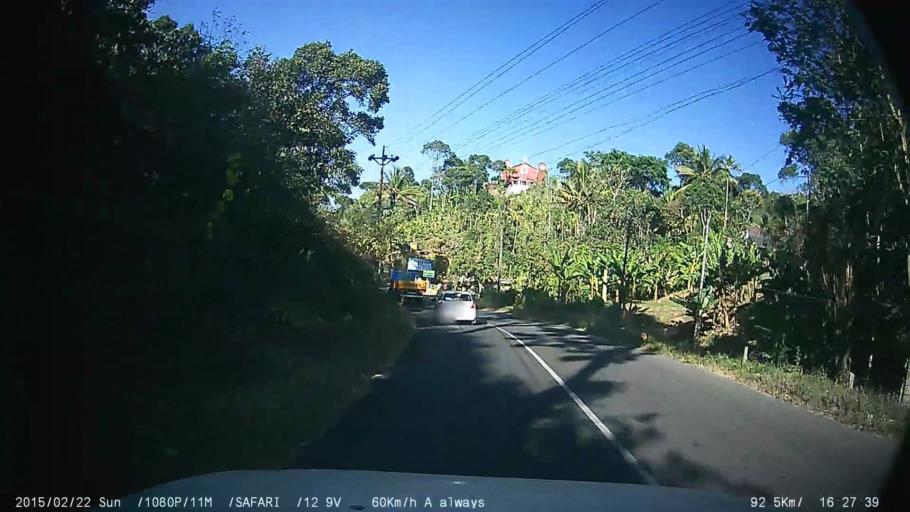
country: IN
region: Tamil Nadu
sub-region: Theni
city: Gudalur
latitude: 9.6056
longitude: 77.1435
